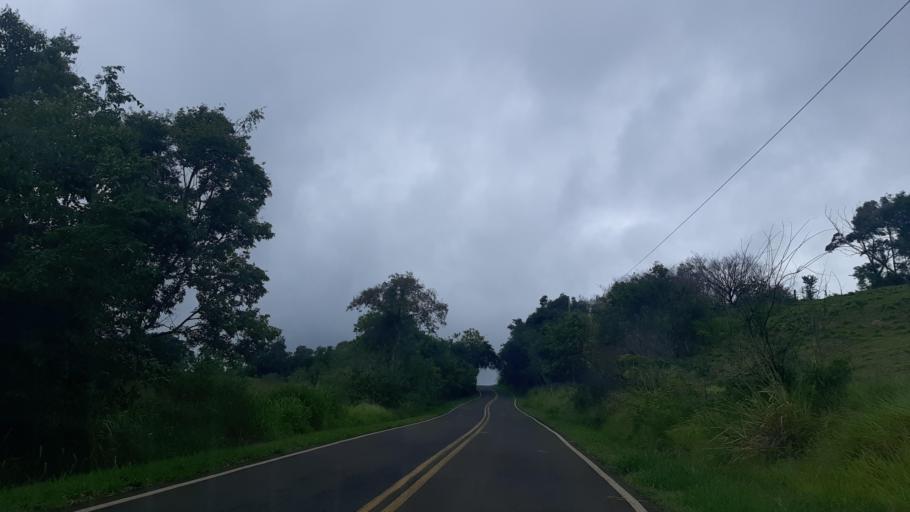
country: BR
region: Parana
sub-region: Ampere
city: Ampere
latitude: -25.9855
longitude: -53.4421
